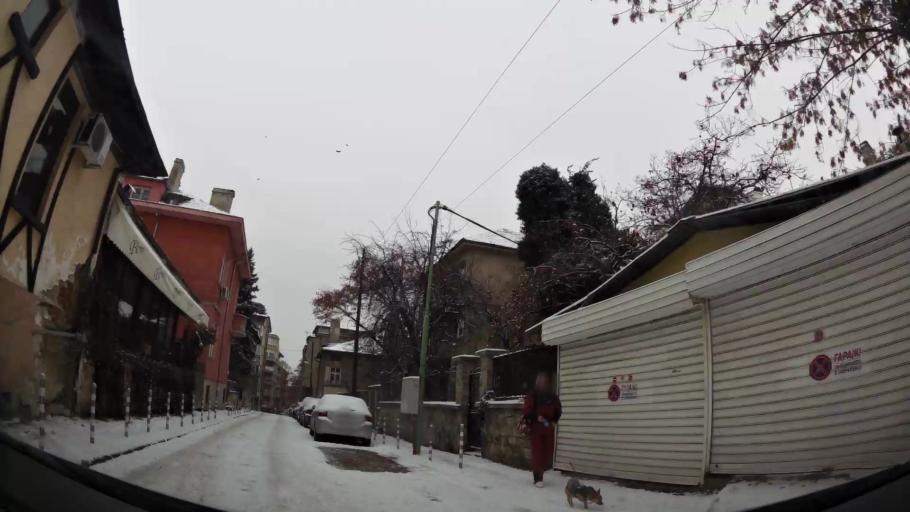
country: BG
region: Sofia-Capital
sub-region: Stolichna Obshtina
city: Sofia
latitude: 42.6898
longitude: 23.3450
